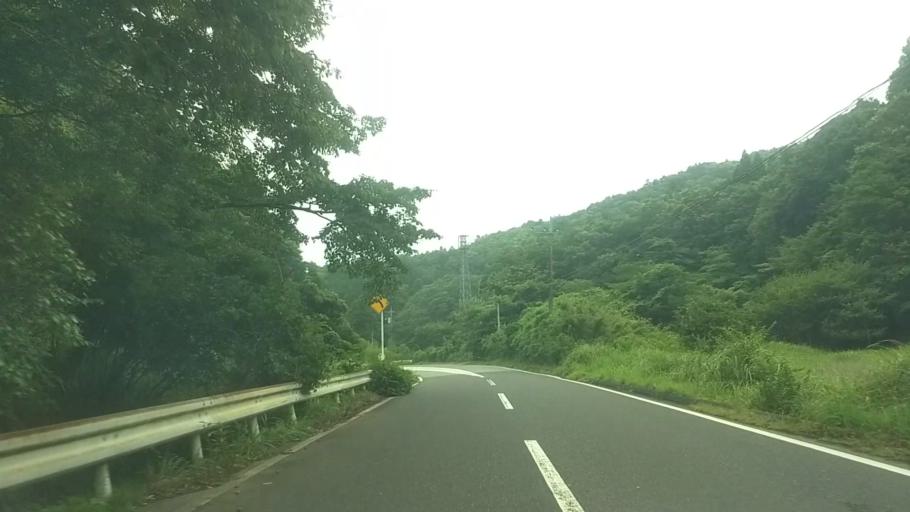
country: JP
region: Chiba
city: Kawaguchi
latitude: 35.2392
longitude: 140.0343
